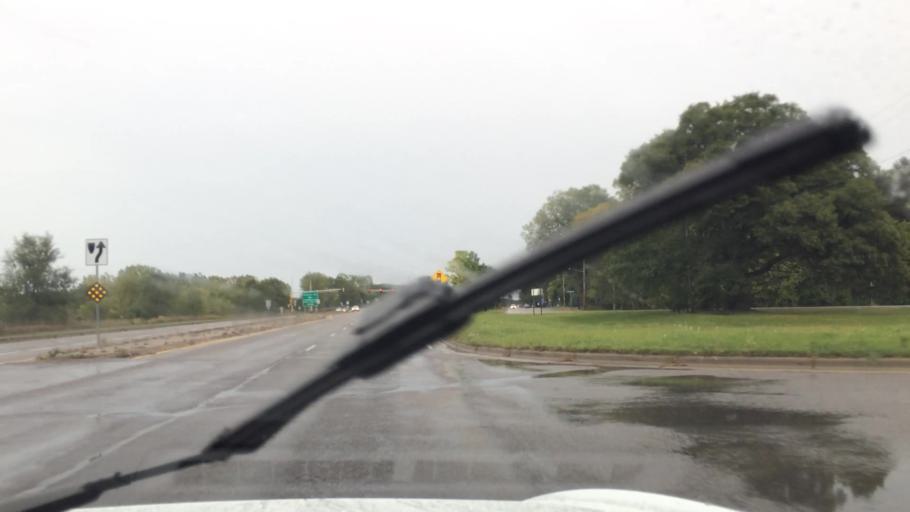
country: US
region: Minnesota
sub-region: Ramsey County
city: Mounds View
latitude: 45.1245
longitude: -93.2214
